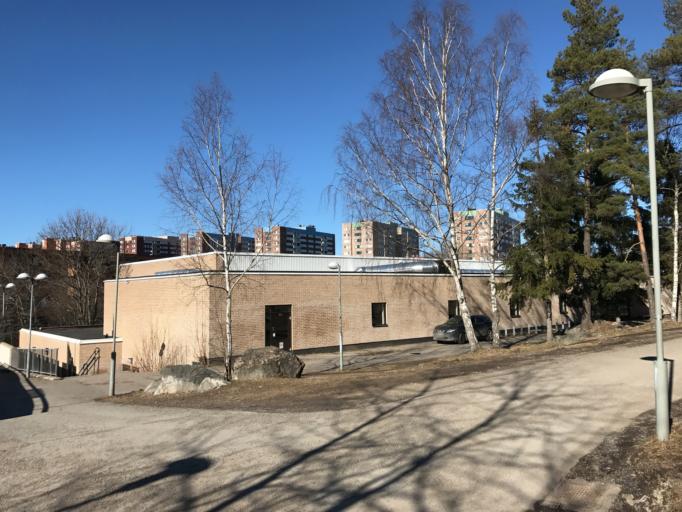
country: SE
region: Stockholm
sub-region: Stockholms Kommun
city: Kista
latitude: 59.4107
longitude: 17.9215
